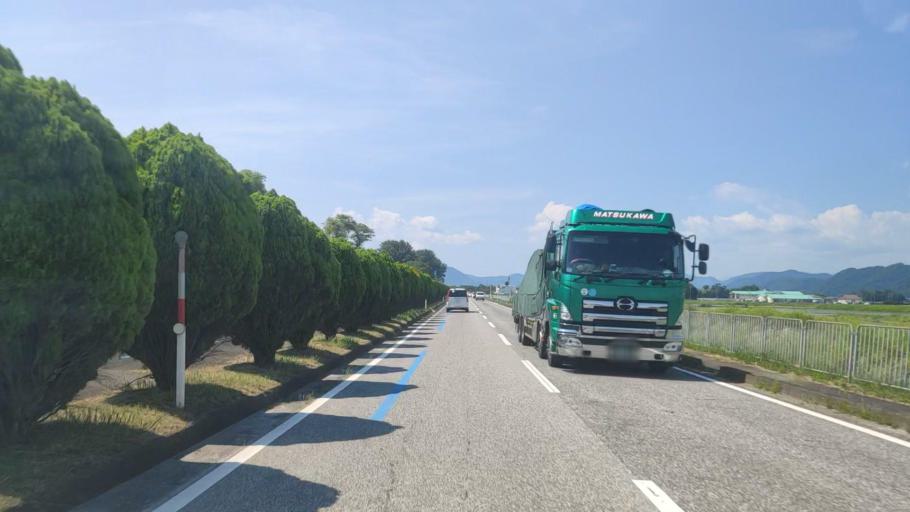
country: JP
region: Shiga Prefecture
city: Nagahama
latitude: 35.4206
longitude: 136.1997
